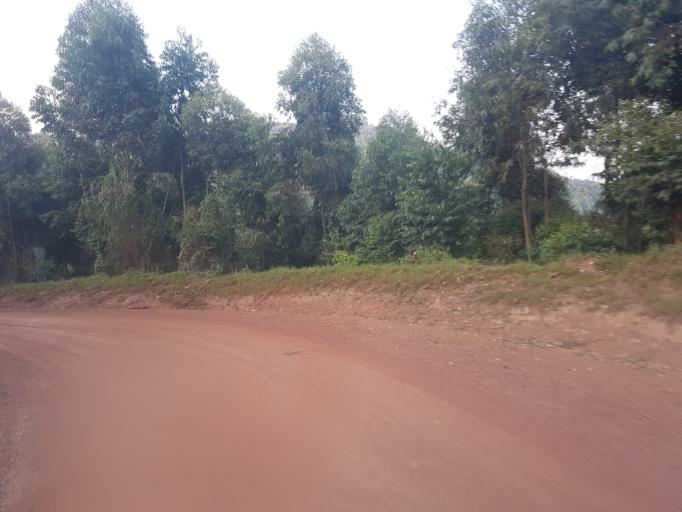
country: UG
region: Western Region
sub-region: Kanungu District
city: Kanungu
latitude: -1.0430
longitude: 29.8847
